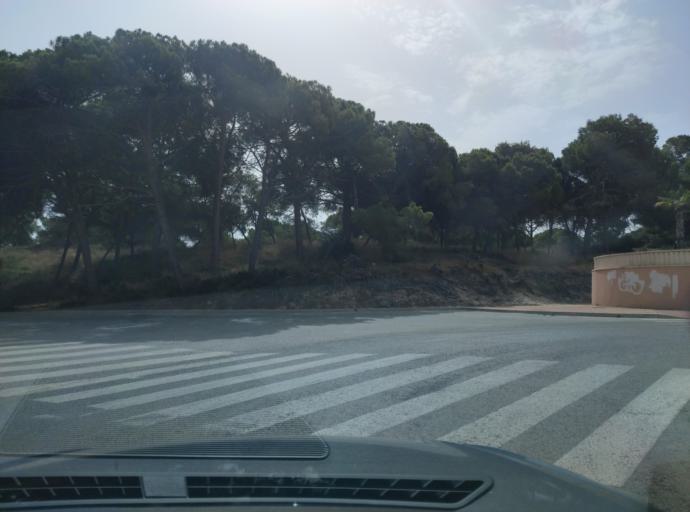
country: ES
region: Valencia
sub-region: Provincia de Alicante
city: Guardamar del Segura
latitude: 38.0977
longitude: -0.6547
